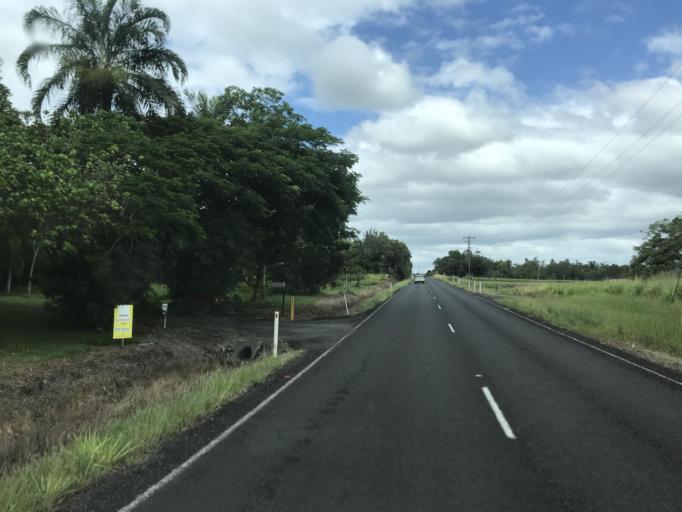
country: AU
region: Queensland
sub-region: Cassowary Coast
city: Innisfail
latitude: -17.8228
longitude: 146.0440
